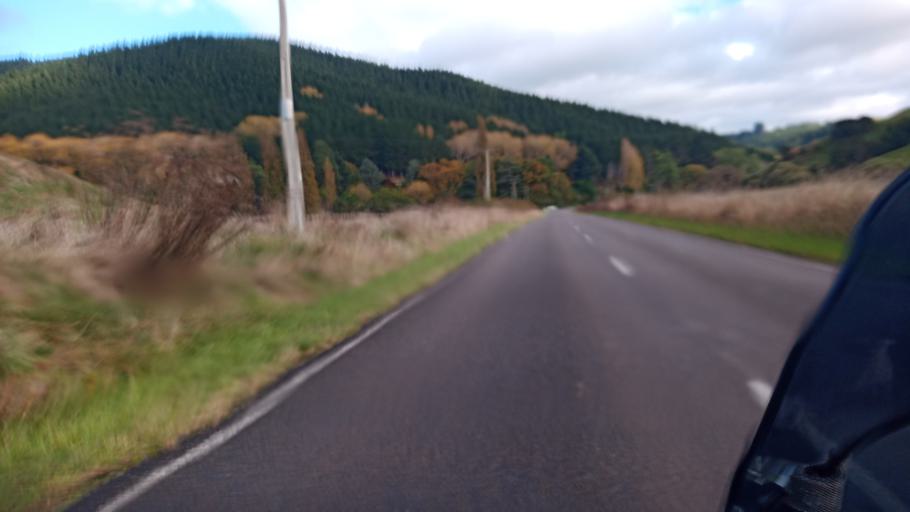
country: NZ
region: Gisborne
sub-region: Gisborne District
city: Gisborne
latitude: -38.5706
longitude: 177.7272
